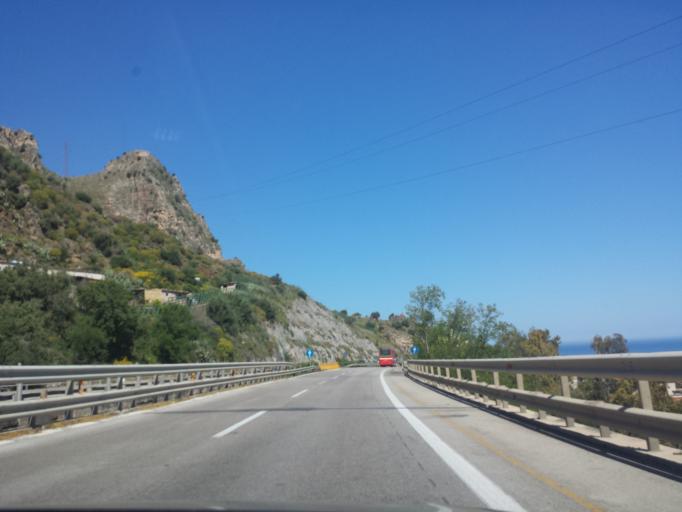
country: IT
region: Sicily
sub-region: Palermo
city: Trabia
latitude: 37.9866
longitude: 13.6564
